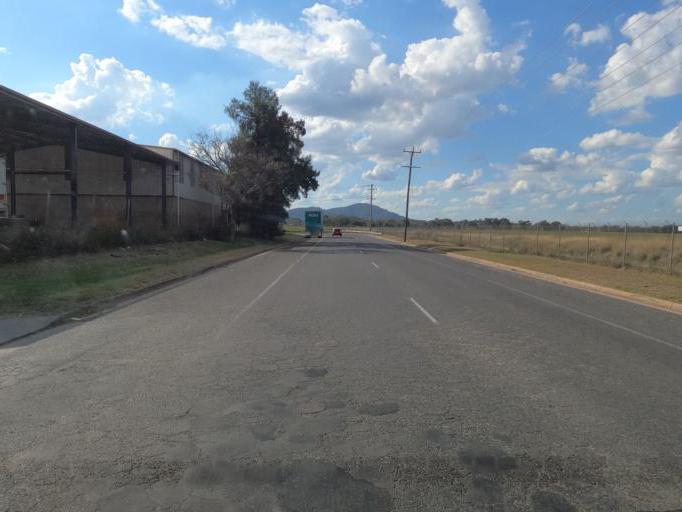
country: AU
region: New South Wales
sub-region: Albury Municipality
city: East Albury
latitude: -36.0722
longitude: 146.9482
